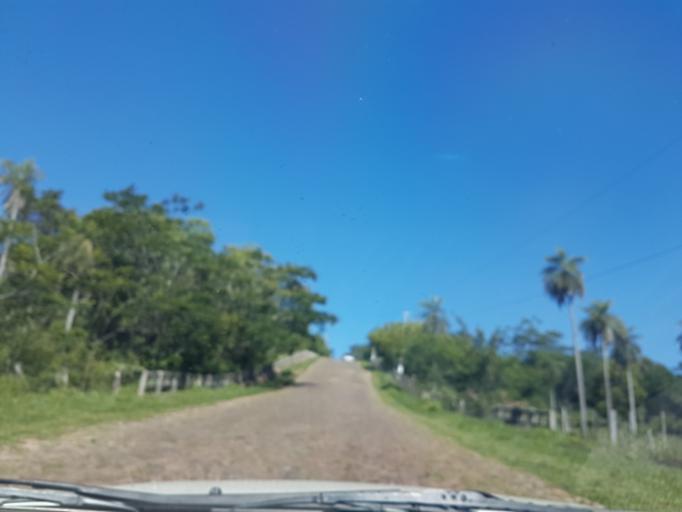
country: PY
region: Cordillera
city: Atyra
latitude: -25.2792
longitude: -57.1509
